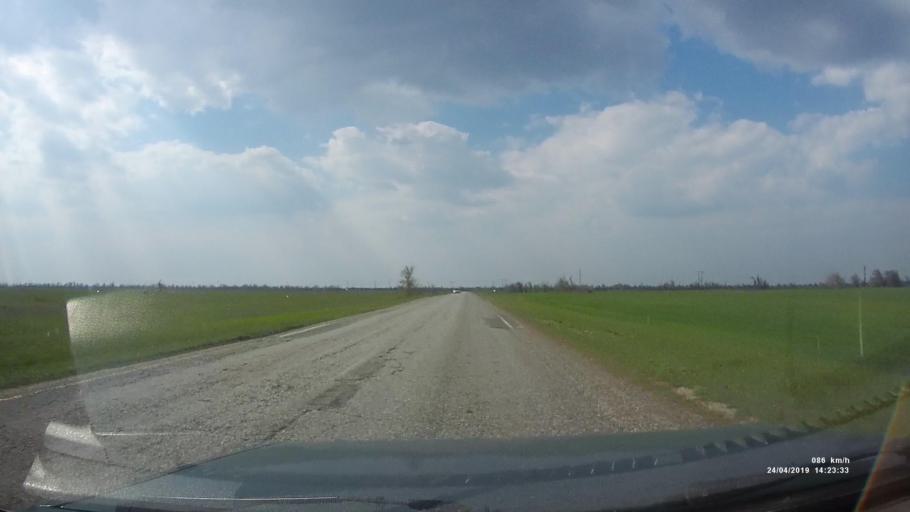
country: RU
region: Kalmykiya
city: Arshan'
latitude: 46.3231
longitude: 44.1127
